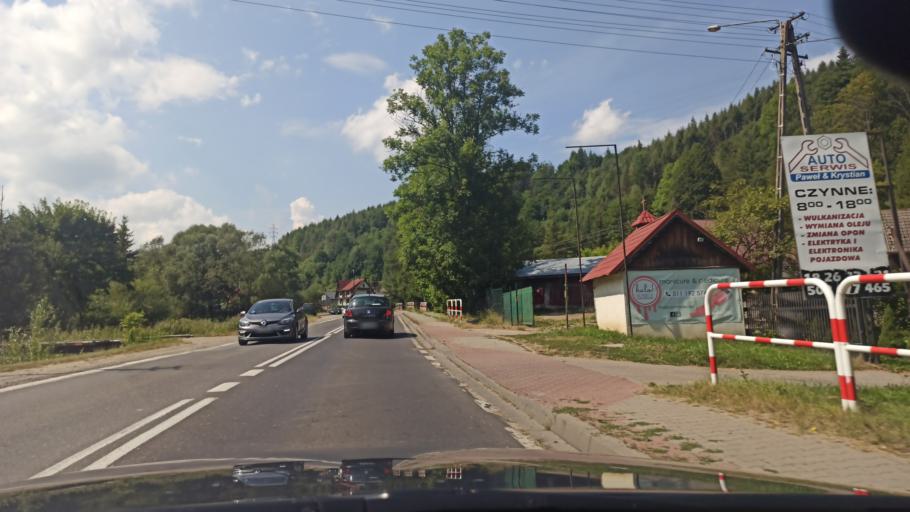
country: PL
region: Lesser Poland Voivodeship
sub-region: Powiat nowotarski
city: Kroscienko nad Dunajcem
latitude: 49.4388
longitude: 20.3891
